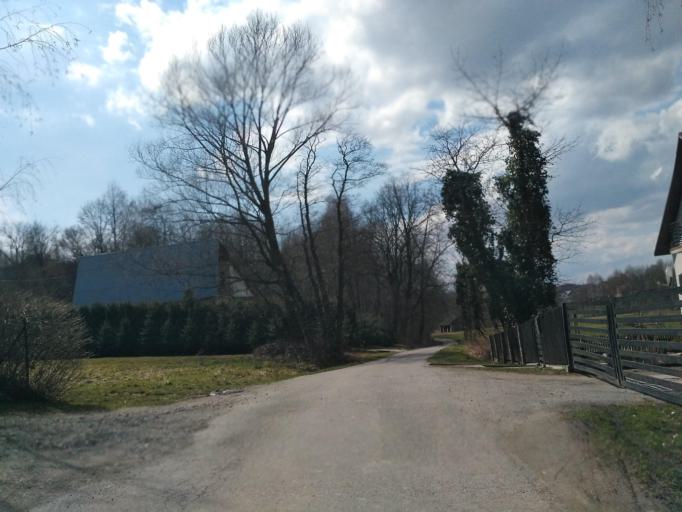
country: PL
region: Subcarpathian Voivodeship
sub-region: Powiat ropczycko-sedziszowski
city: Iwierzyce
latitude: 49.9943
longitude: 21.7424
